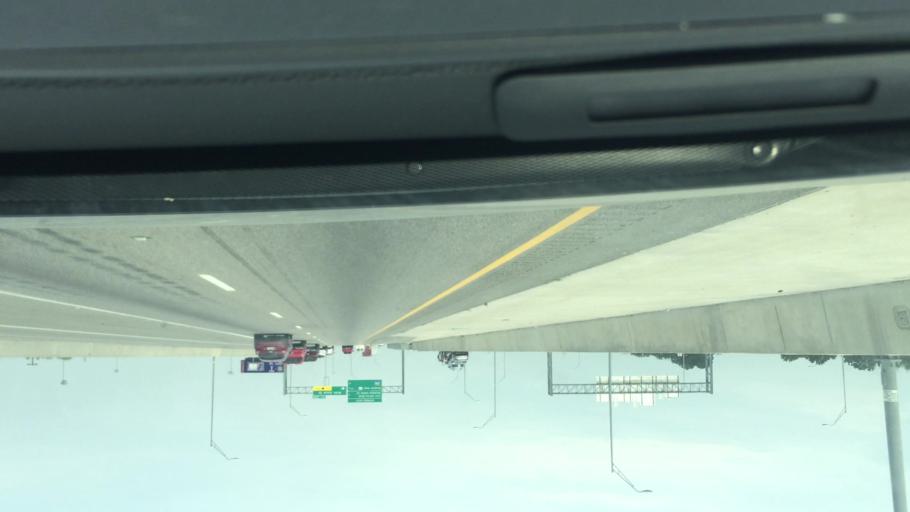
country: US
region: Texas
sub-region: Tarrant County
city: North Richland Hills
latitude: 32.8378
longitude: -97.2258
